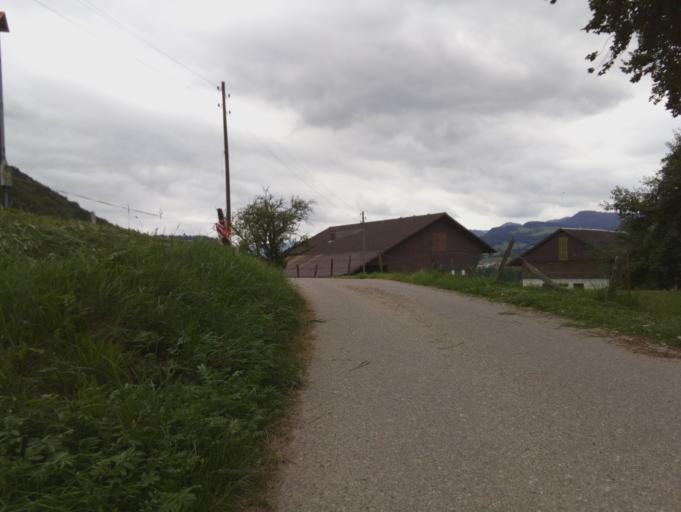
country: CH
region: Saint Gallen
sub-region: Wahlkreis Toggenburg
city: Buetschwil
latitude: 47.3619
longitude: 9.0843
